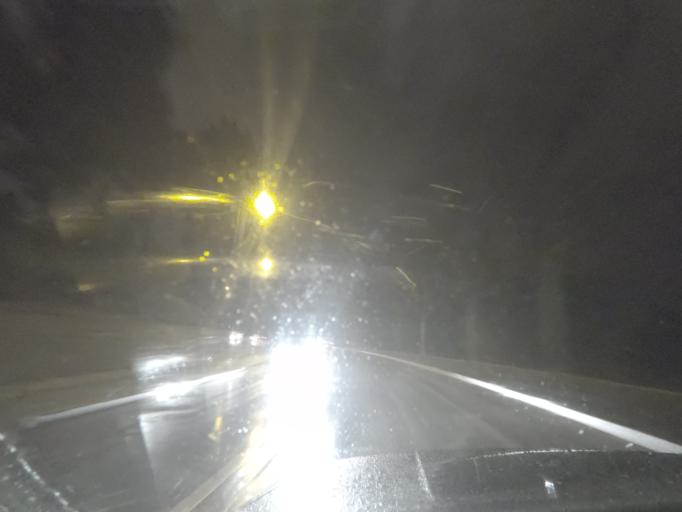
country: PT
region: Vila Real
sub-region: Vila Real
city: Vila Real
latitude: 41.3037
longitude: -7.7339
